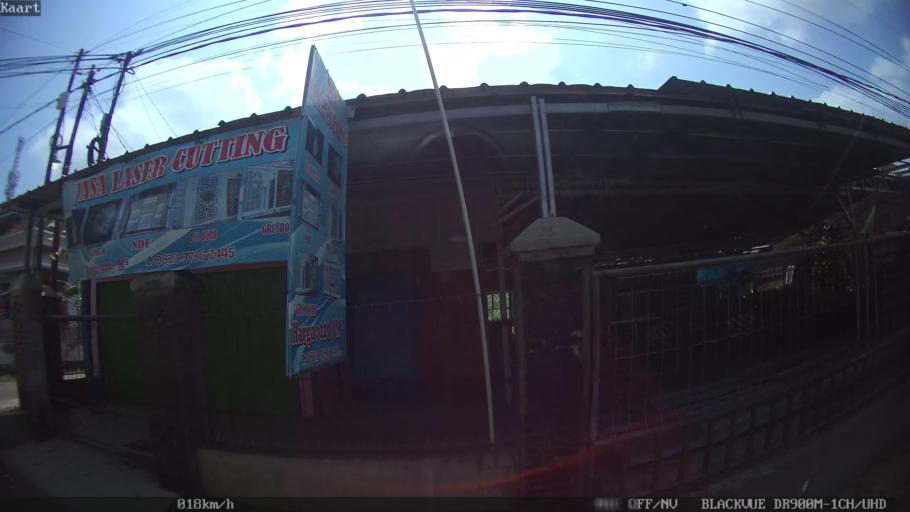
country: ID
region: Lampung
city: Kedaton
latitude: -5.3603
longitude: 105.2795
